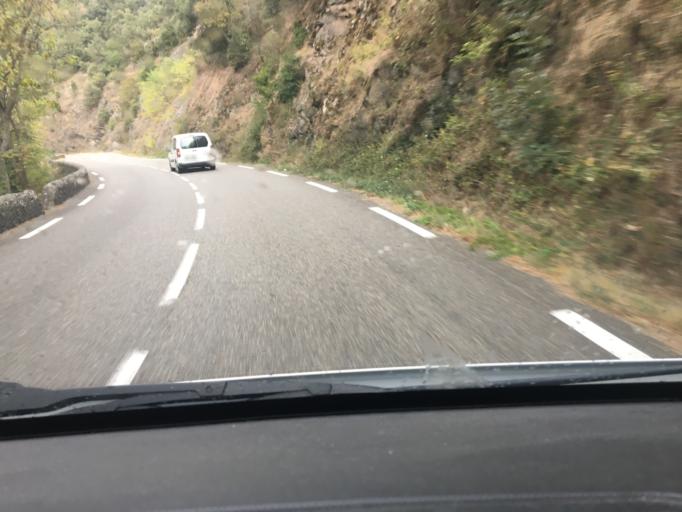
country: FR
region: Rhone-Alpes
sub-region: Departement de l'Ardeche
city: Saint-Jean-de-Muzols
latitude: 45.0595
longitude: 4.7862
